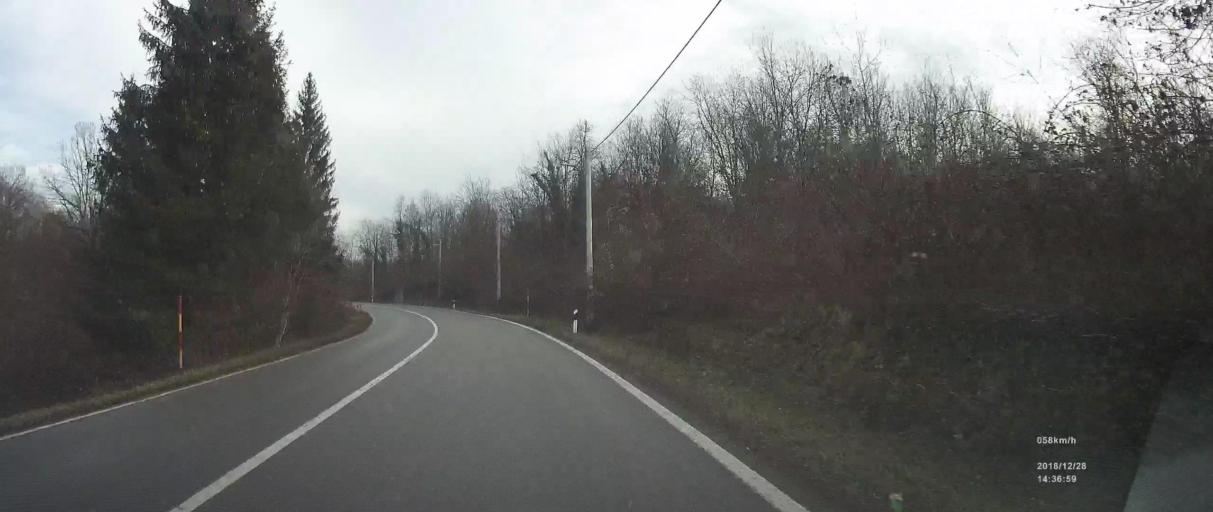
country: HR
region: Primorsko-Goranska
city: Vrbovsko
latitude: 45.4209
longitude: 15.2038
